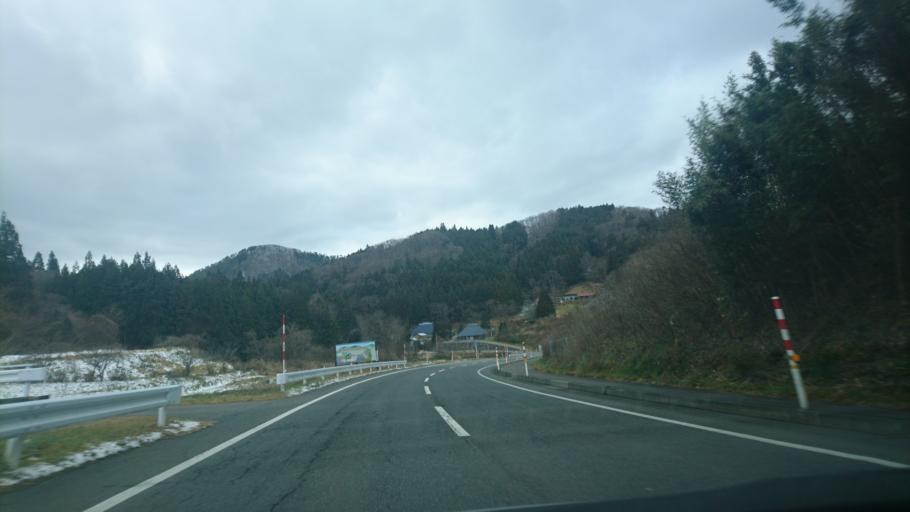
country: JP
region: Iwate
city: Mizusawa
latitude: 39.1814
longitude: 141.2954
